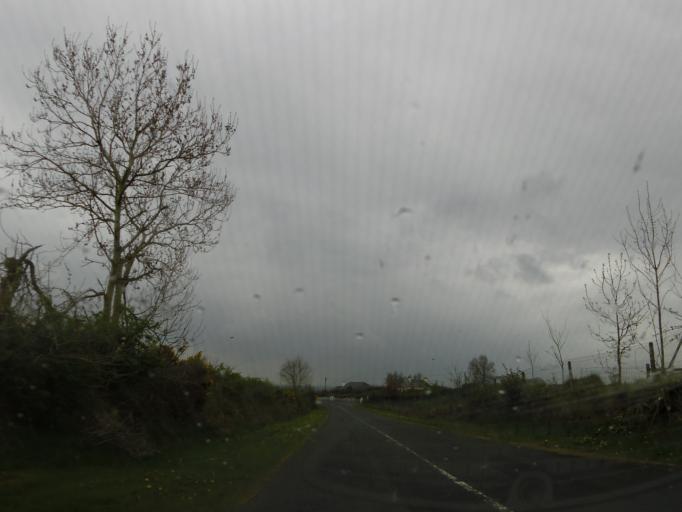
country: IE
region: Connaught
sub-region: Maigh Eo
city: Claremorris
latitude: 53.7630
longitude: -8.9647
